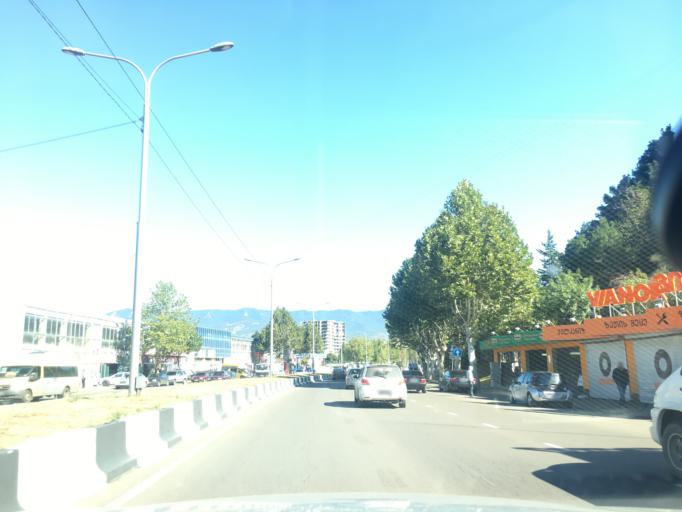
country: GE
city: Zahesi
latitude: 41.7789
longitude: 44.7961
